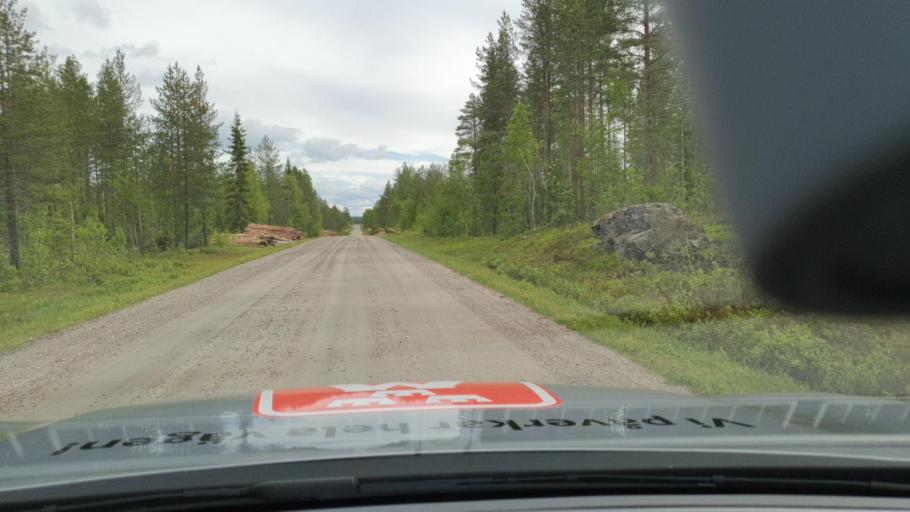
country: FI
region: Lapland
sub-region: Torniolaakso
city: Ylitornio
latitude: 65.9497
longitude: 23.5585
